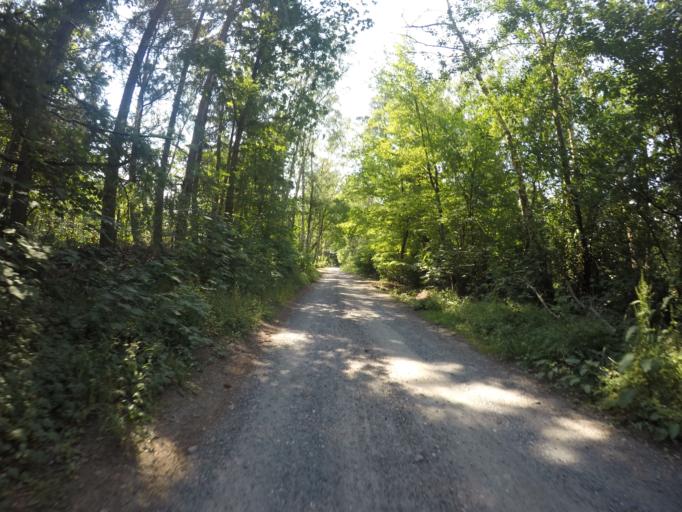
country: DE
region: Lower Saxony
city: Buchholz in der Nordheide
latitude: 53.3086
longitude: 9.8191
